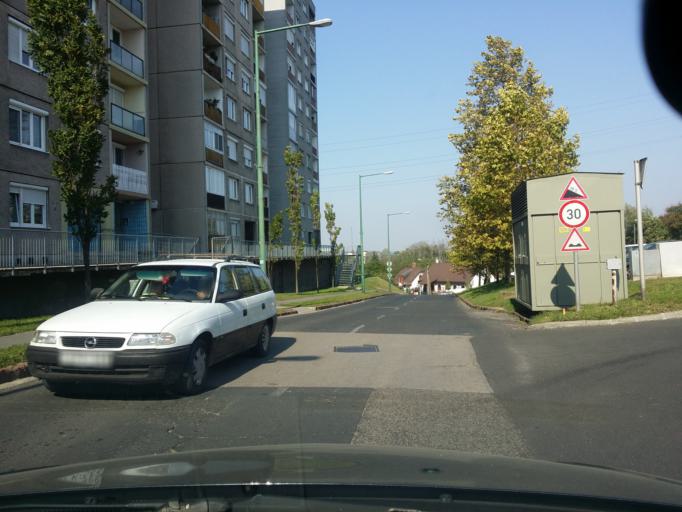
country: HU
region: Fejer
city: dunaujvaros
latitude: 46.9742
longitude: 18.9349
